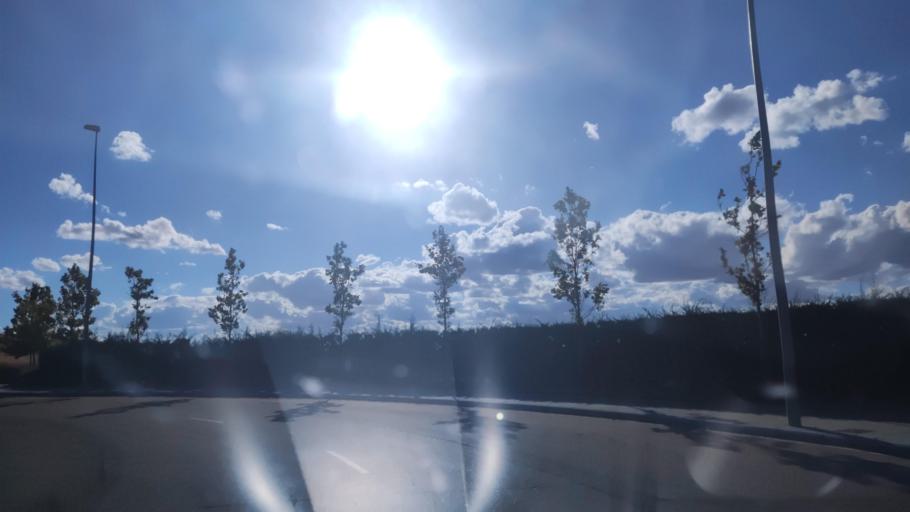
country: ES
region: Castille and Leon
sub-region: Provincia de Salamanca
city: Villamayor
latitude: 40.9691
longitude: -5.6951
